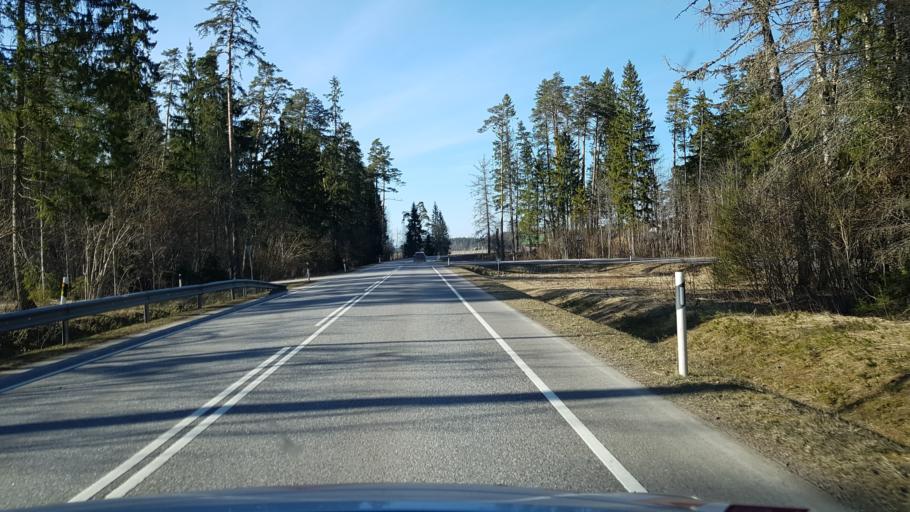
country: EE
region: Laeaene-Virumaa
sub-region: Vinni vald
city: Vinni
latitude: 59.1769
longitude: 26.5785
